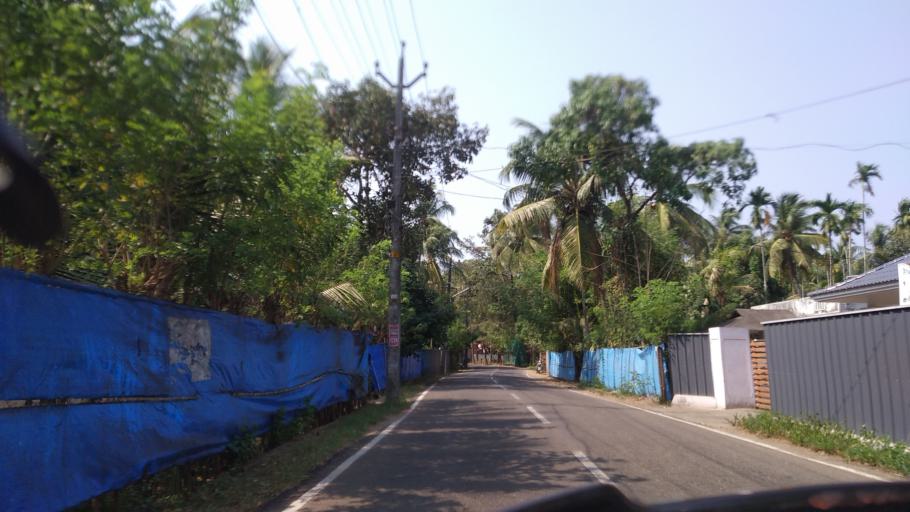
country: IN
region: Kerala
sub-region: Thrissur District
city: Thanniyam
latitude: 10.4021
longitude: 76.0958
